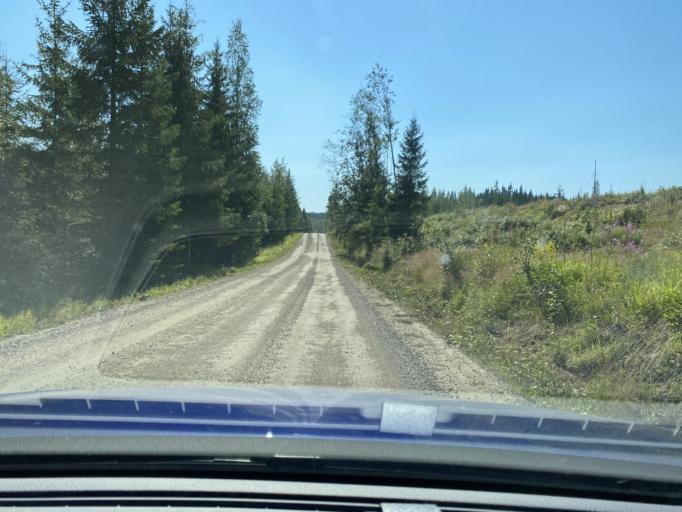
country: FI
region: Central Finland
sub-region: Jyvaeskylae
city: Korpilahti
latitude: 61.8695
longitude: 25.4211
